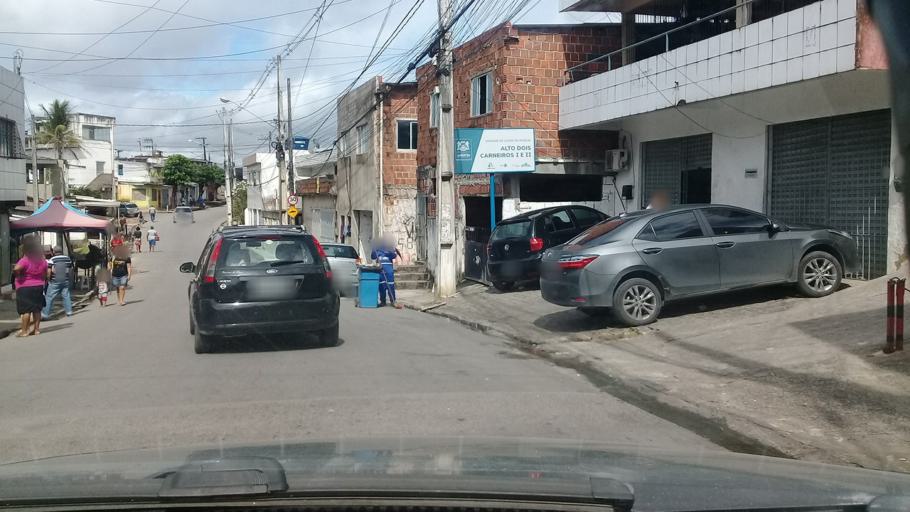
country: BR
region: Pernambuco
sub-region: Jaboatao Dos Guararapes
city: Jaboatao dos Guararapes
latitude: -8.1098
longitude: -34.9631
